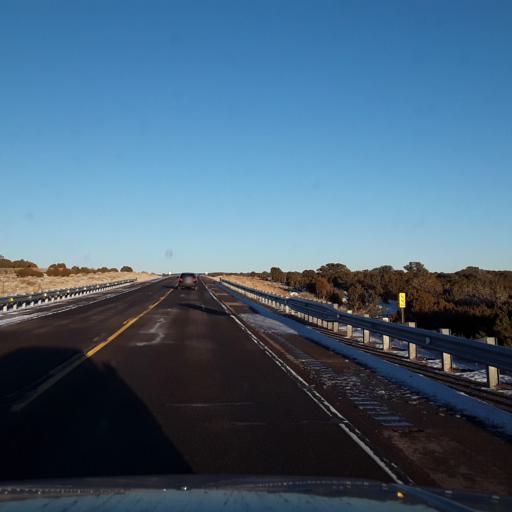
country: US
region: New Mexico
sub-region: Lincoln County
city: Carrizozo
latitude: 34.2312
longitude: -105.6272
